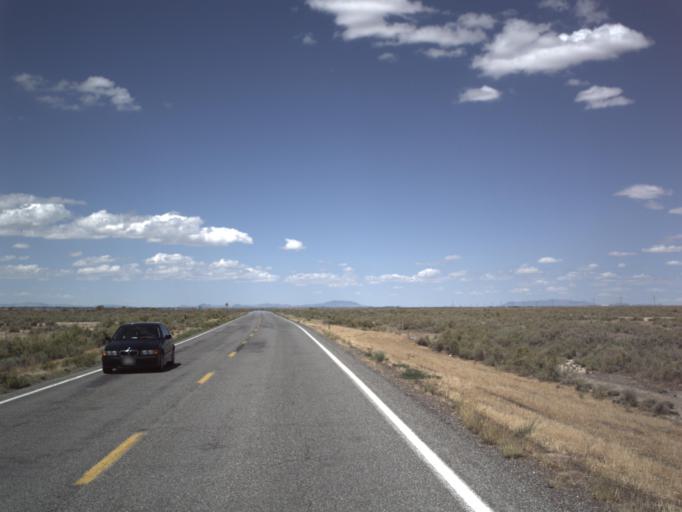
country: US
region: Utah
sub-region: Millard County
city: Delta
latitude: 39.2574
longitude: -112.4438
